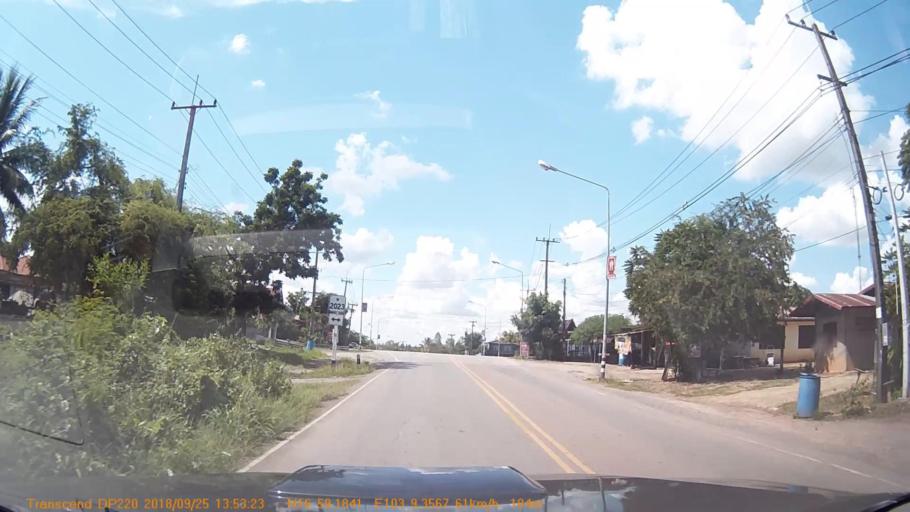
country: TH
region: Changwat Udon Thani
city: Si That
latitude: 16.9865
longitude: 103.1559
